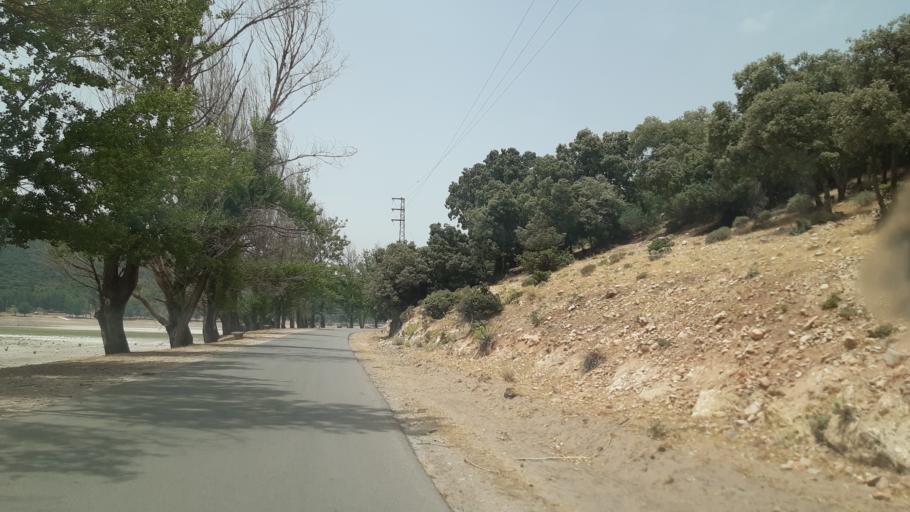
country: MA
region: Meknes-Tafilalet
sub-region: Ifrane
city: Ifrane
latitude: 33.6550
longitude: -5.0361
